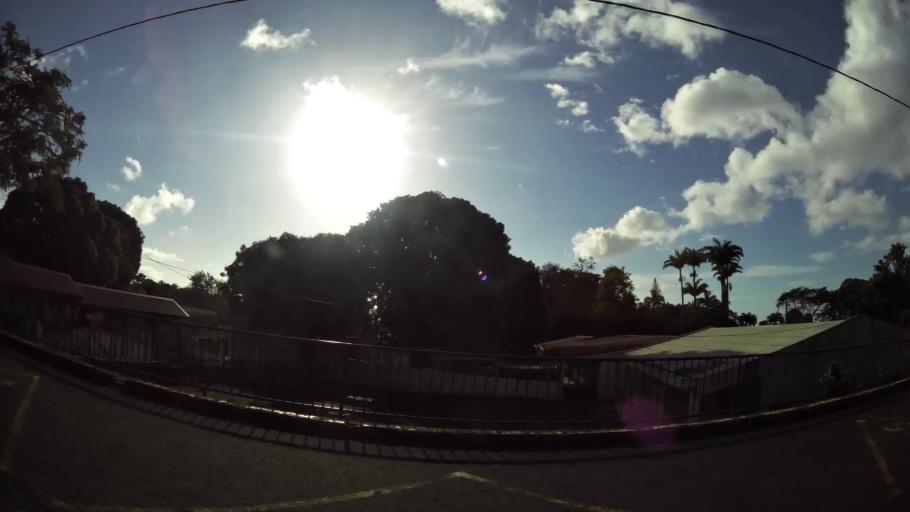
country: GP
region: Guadeloupe
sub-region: Guadeloupe
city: Pointe-Noire
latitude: 16.2558
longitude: -61.7897
